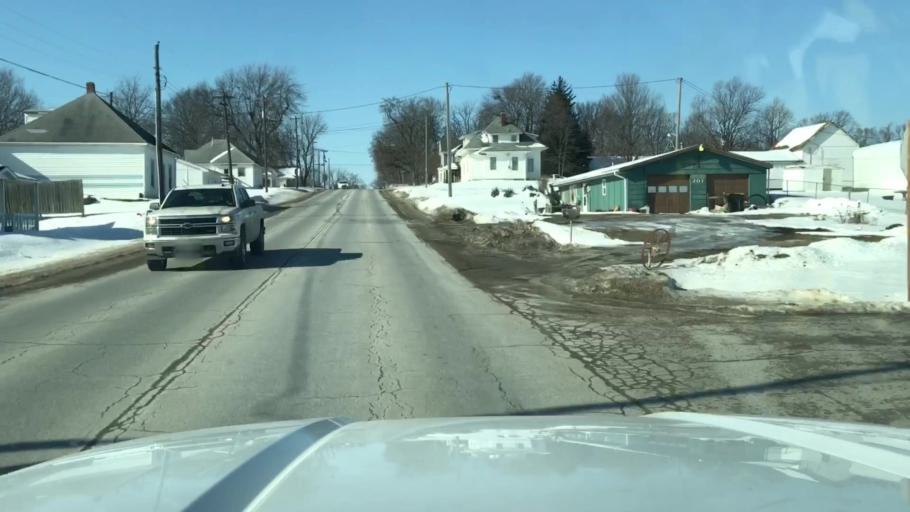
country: US
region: Missouri
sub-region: Andrew County
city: Savannah
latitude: 39.9467
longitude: -94.8258
